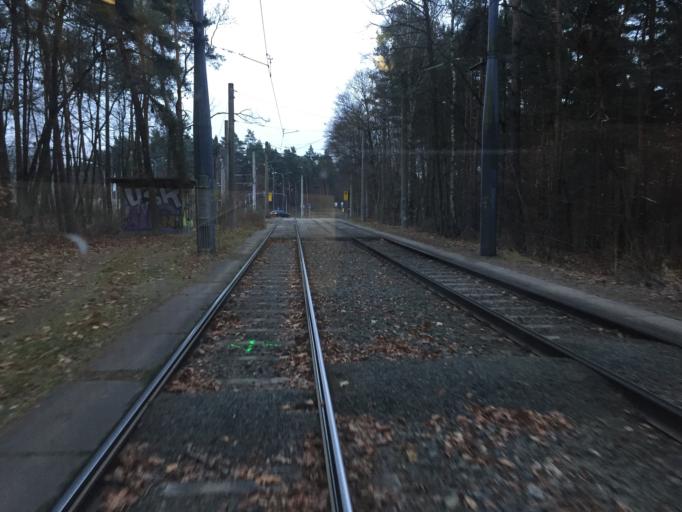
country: DE
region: Saxony
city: Albertstadt
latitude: 51.1035
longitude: 13.7693
